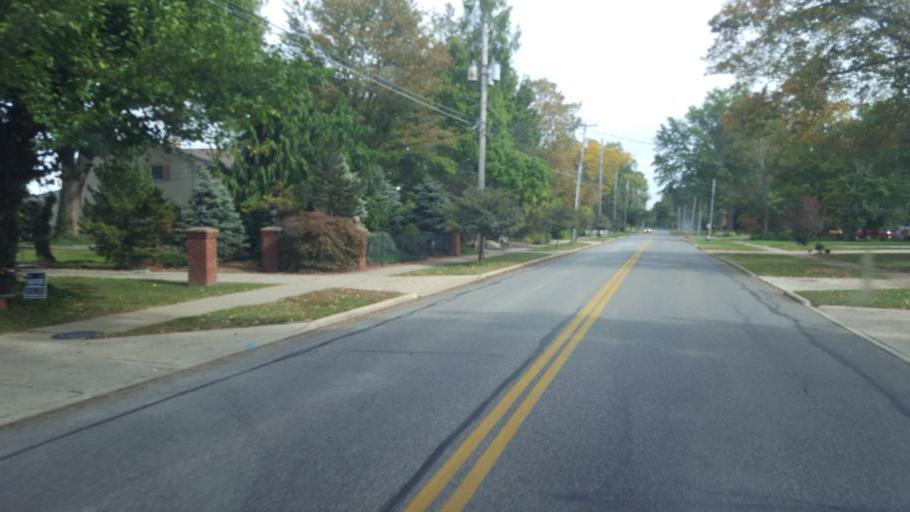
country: US
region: Ohio
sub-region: Cuyahoga County
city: Bay Village
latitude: 41.4949
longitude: -81.9541
